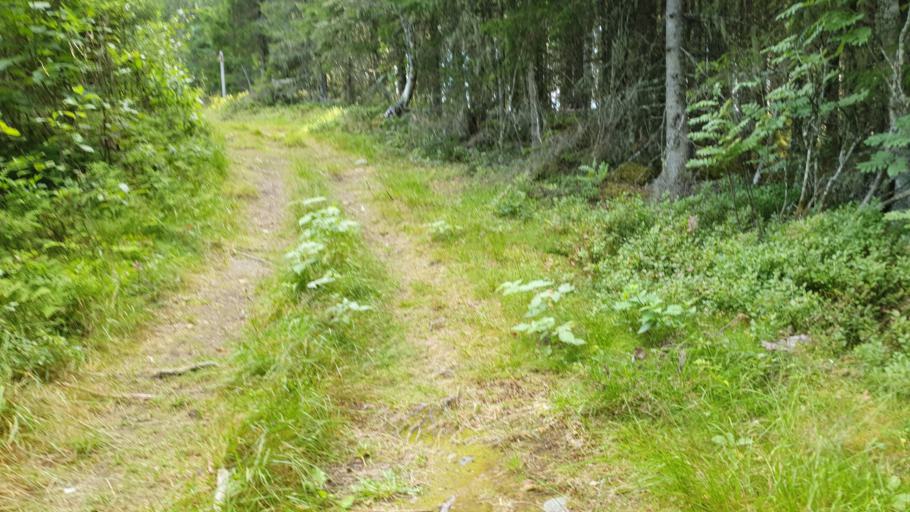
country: NO
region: Nord-Trondelag
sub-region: Levanger
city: Levanger
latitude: 63.6941
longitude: 11.2756
